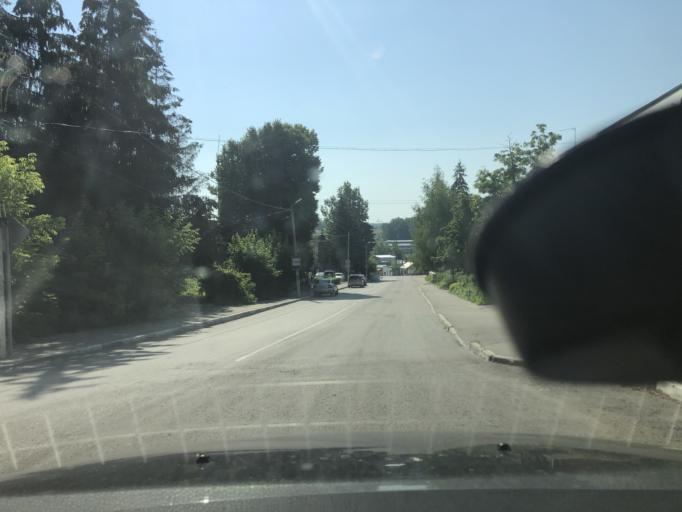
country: RU
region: Tula
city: Dubna
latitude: 54.1523
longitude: 36.9610
